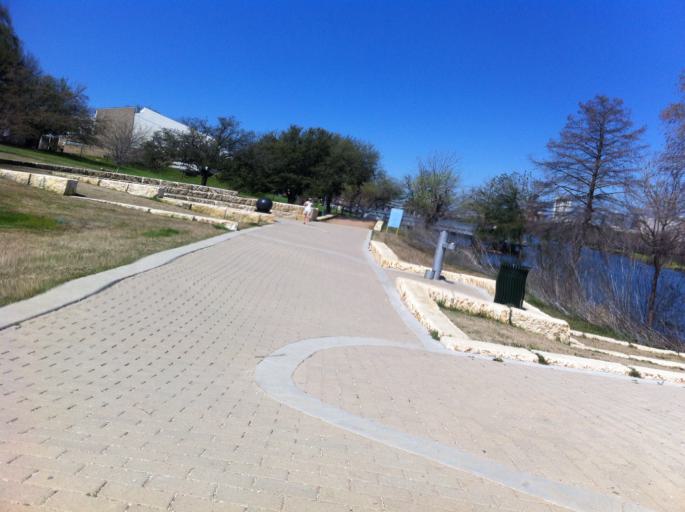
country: US
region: Texas
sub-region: Travis County
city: Austin
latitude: 30.2450
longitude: -97.7246
